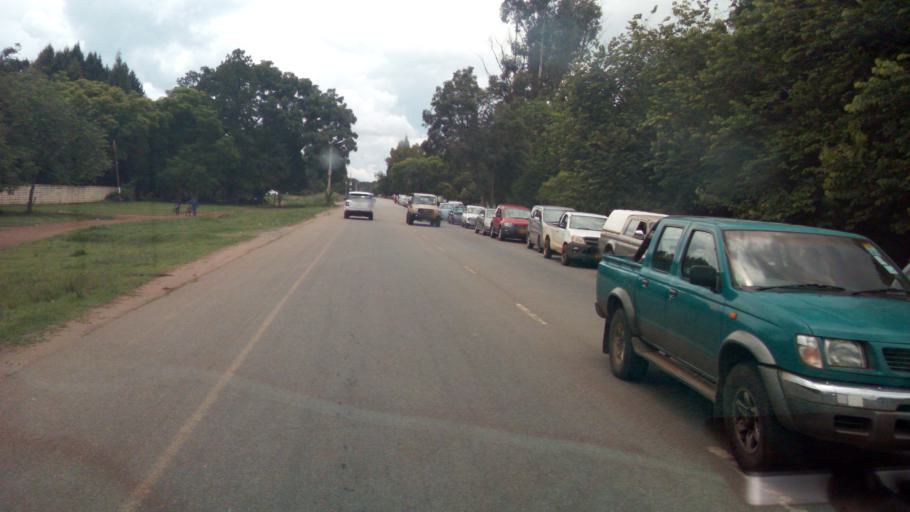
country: ZW
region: Harare
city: Harare
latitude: -17.7513
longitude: 31.0176
